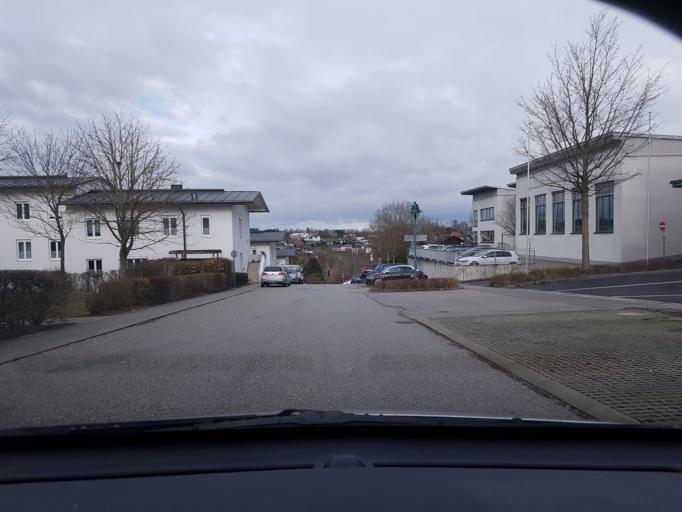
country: AT
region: Upper Austria
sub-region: Politischer Bezirk Linz-Land
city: Sankt Florian
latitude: 48.1589
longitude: 14.3392
